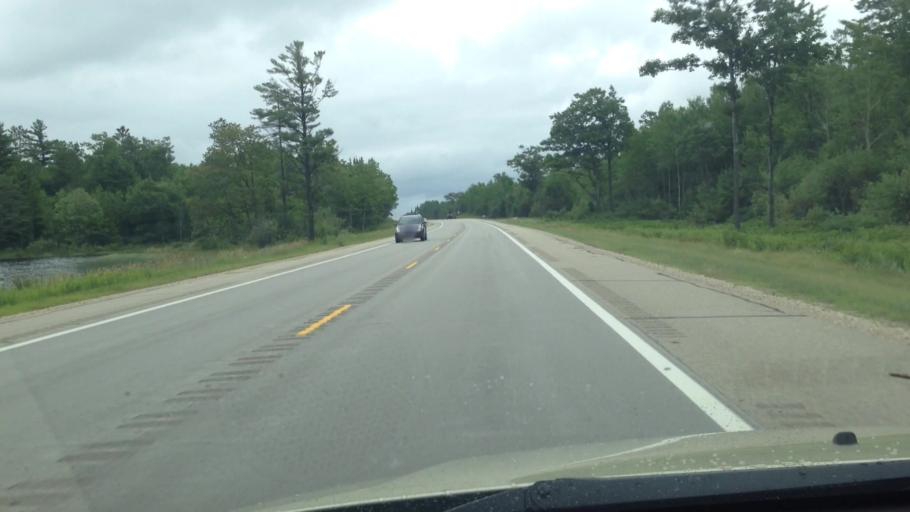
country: US
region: Michigan
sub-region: Schoolcraft County
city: Manistique
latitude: 45.9099
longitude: -86.4483
